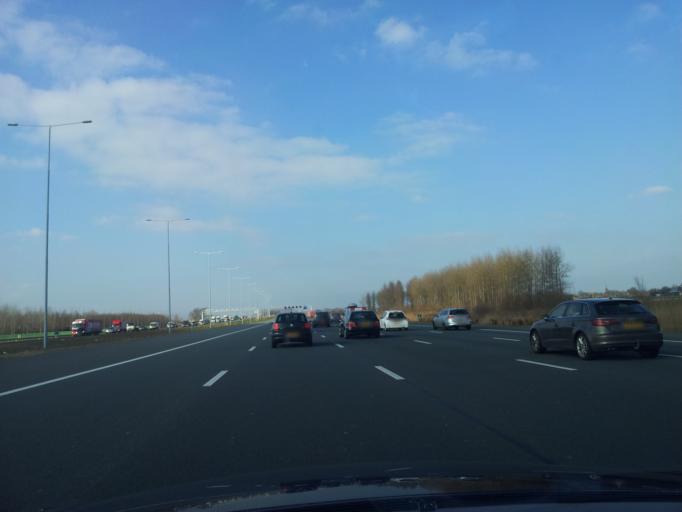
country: NL
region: North Holland
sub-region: Gemeente Amsterdam
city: Amsterdam-Zuidoost
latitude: 52.2539
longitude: 4.9679
